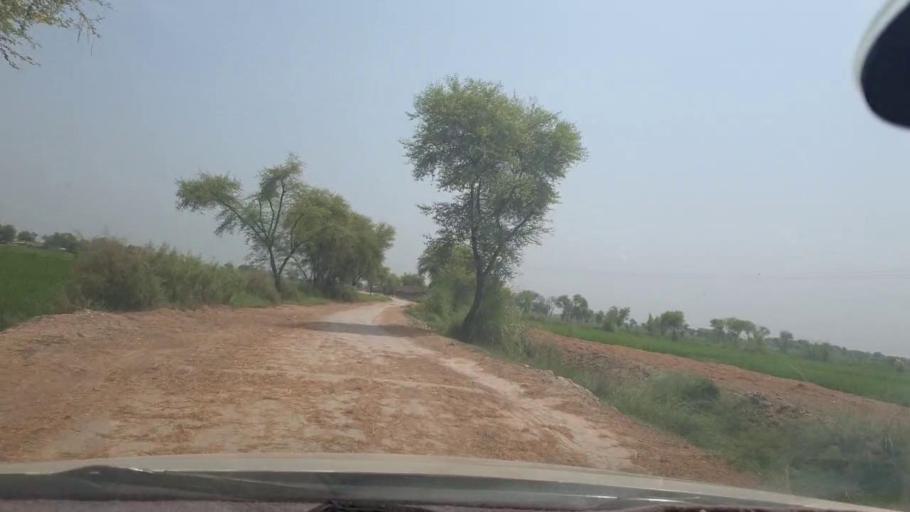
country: PK
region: Sindh
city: Jacobabad
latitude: 28.1765
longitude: 68.3844
